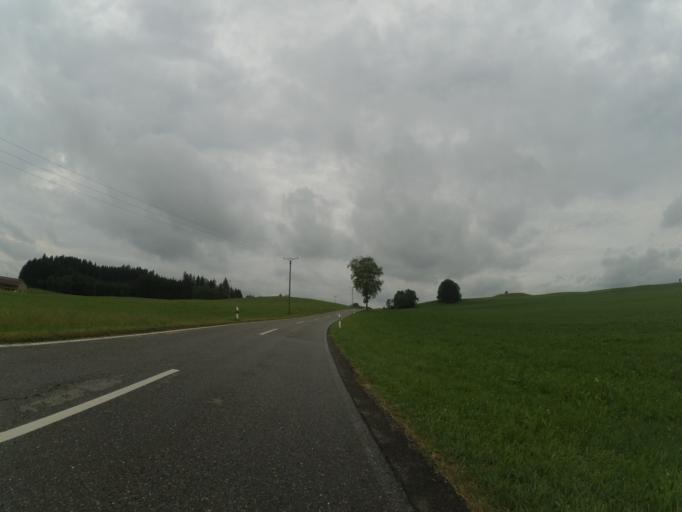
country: DE
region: Baden-Wuerttemberg
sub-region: Tuebingen Region
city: Kisslegg
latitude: 47.7444
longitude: 9.8514
